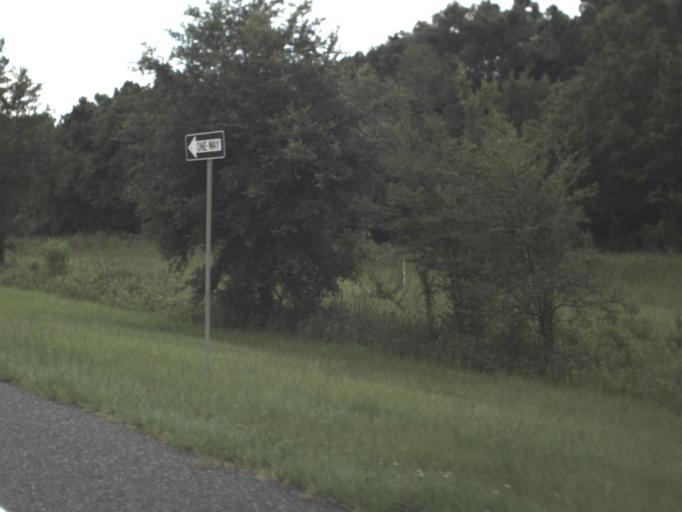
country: US
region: Florida
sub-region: Levy County
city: Williston Highlands
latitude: 29.2454
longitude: -82.7183
